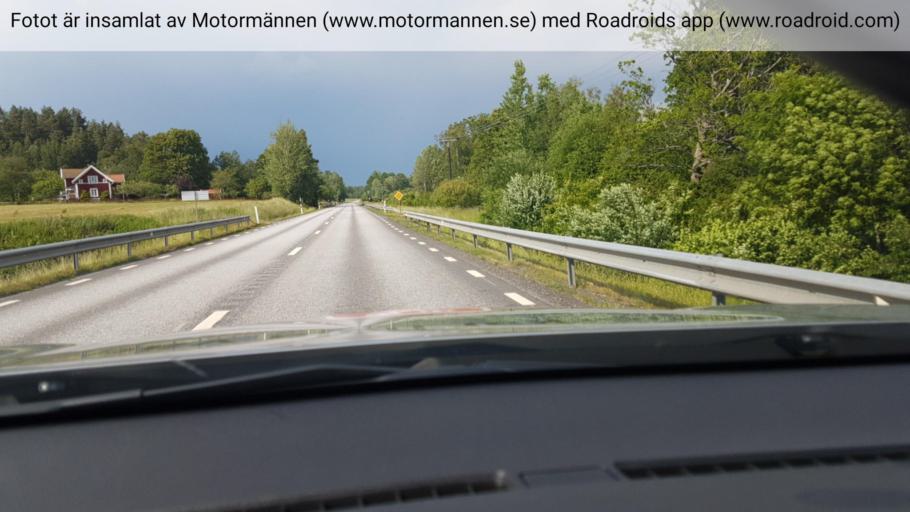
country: SE
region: Joenkoeping
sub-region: Habo Kommun
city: Habo
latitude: 58.0449
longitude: 14.1825
